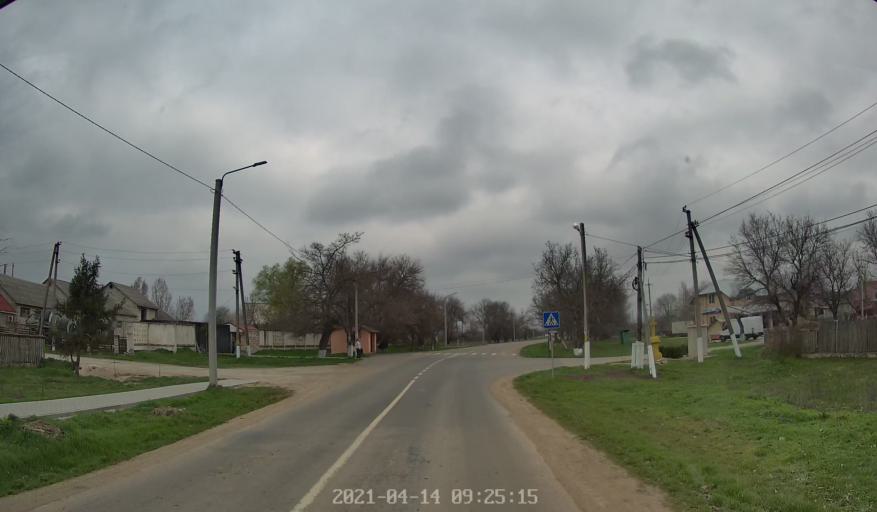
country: MD
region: Chisinau
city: Vadul lui Voda
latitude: 47.1143
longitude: 29.1112
